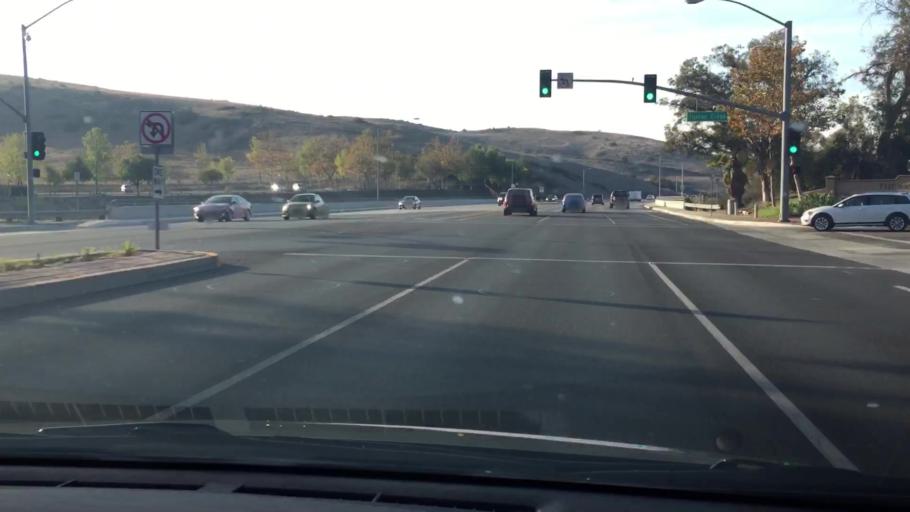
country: US
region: California
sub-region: Orange County
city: Las Flores
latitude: 33.6109
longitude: -117.6172
